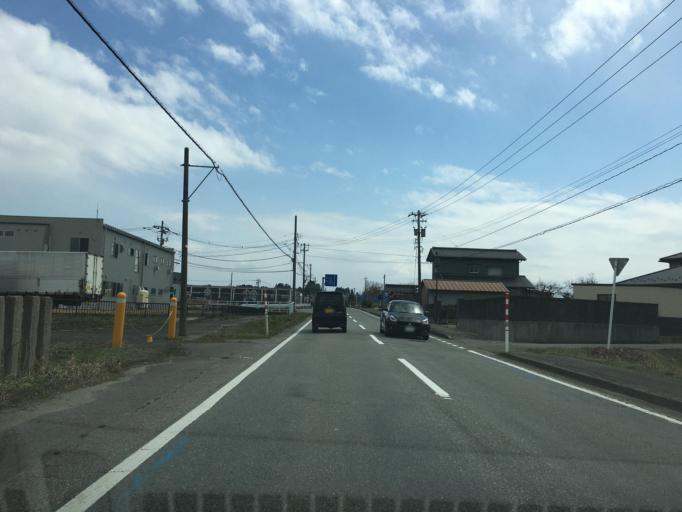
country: JP
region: Toyama
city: Kuragaki-kosugi
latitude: 36.6772
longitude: 137.1247
